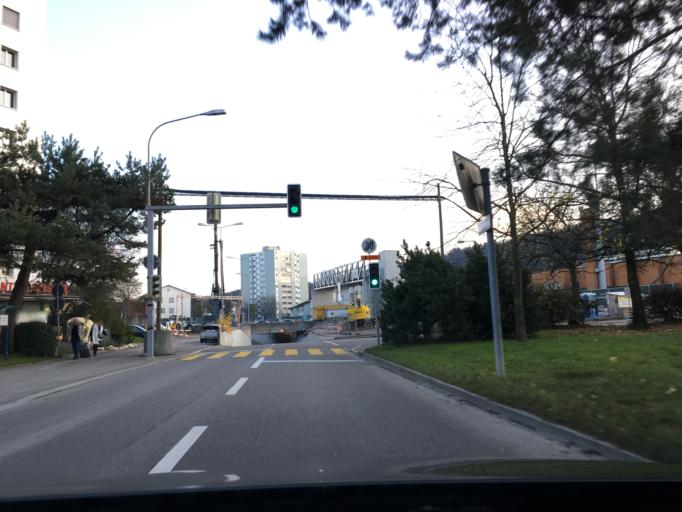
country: CH
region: Zurich
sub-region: Bezirk Zuerich
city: Zuerich (Kreis 12) / Saatlen
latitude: 47.4083
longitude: 8.5652
